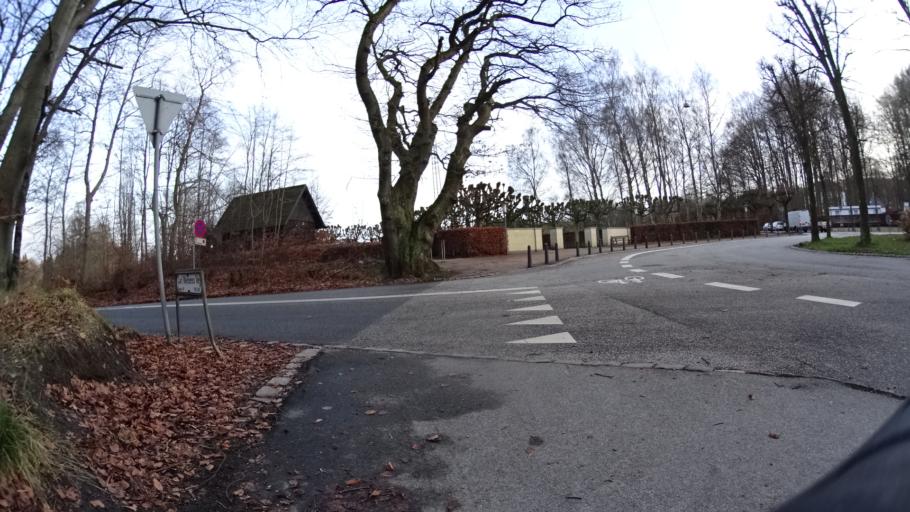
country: DK
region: Central Jutland
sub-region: Arhus Kommune
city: Arhus
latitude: 56.1221
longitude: 10.1809
